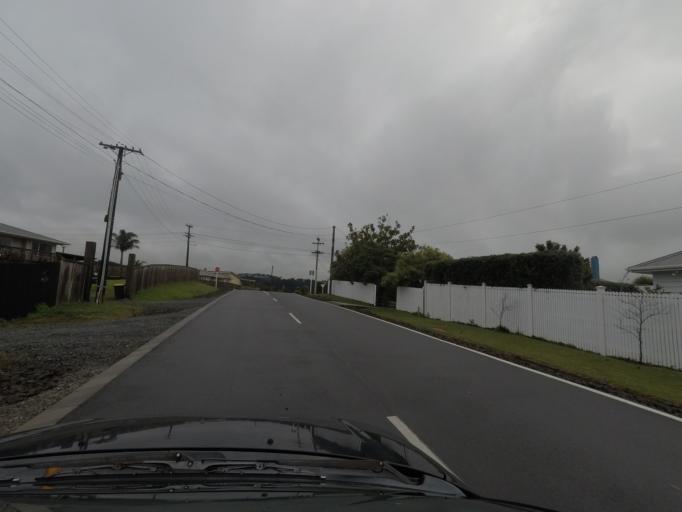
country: NZ
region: Auckland
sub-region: Auckland
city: Rosebank
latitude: -36.7598
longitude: 174.5950
